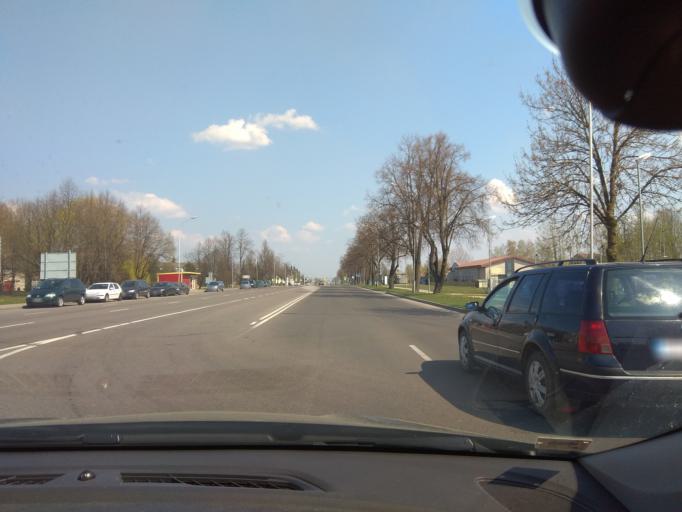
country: LT
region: Marijampoles apskritis
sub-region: Marijampole Municipality
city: Marijampole
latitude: 54.5767
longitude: 23.3712
